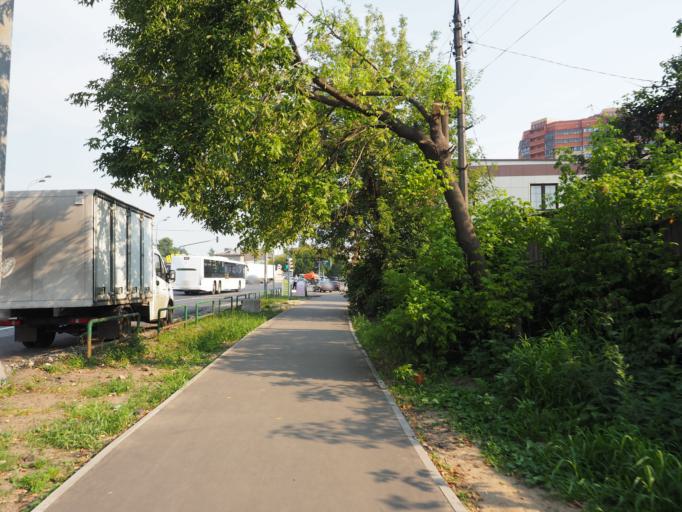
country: RU
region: Moskovskaya
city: Oktyabr'skiy
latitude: 55.6116
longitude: 37.9745
